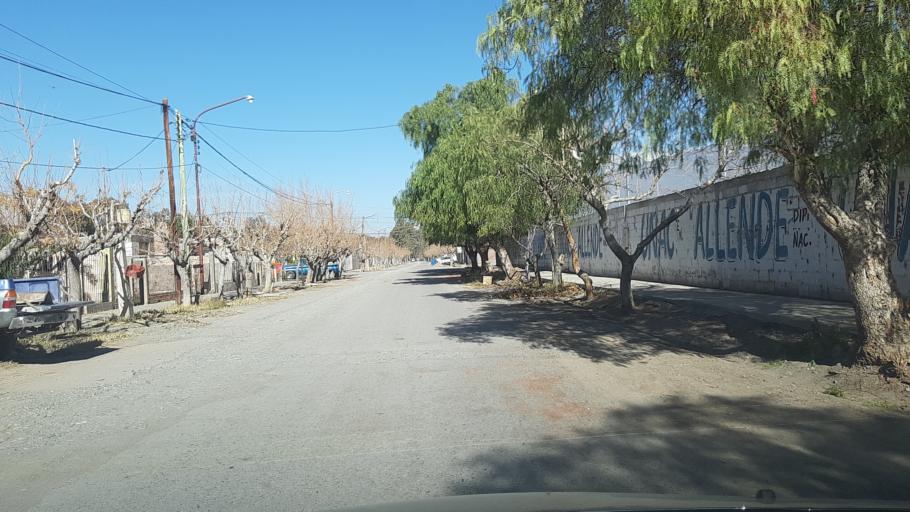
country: AR
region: San Juan
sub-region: Departamento de Zonda
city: Zonda
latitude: -31.5473
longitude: -68.7273
